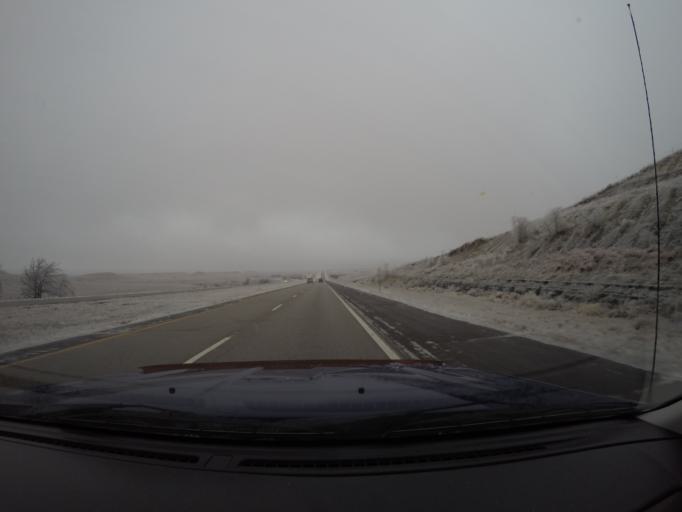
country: US
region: Kansas
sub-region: Riley County
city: Manhattan
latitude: 39.0763
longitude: -96.5382
